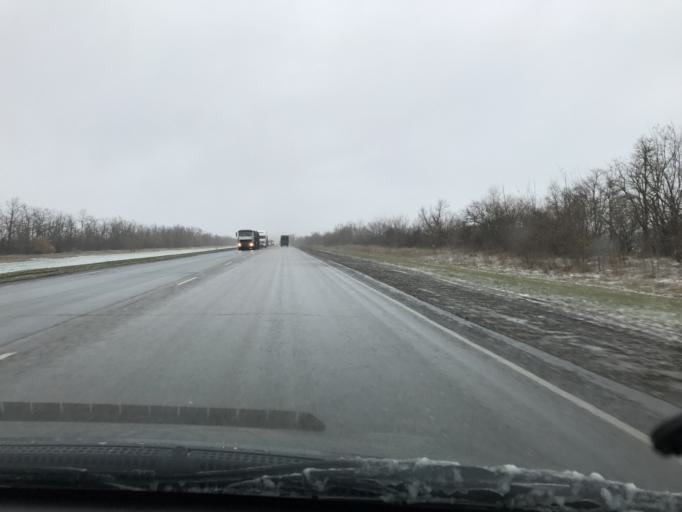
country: RU
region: Rostov
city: Mechetinskaya
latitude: 46.7313
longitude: 40.4782
